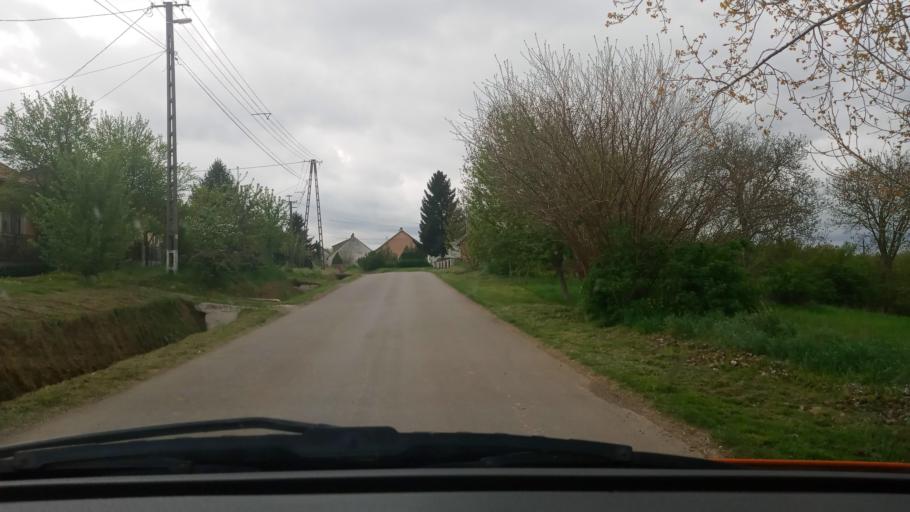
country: HU
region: Baranya
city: Boly
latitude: 45.9910
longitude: 18.5163
